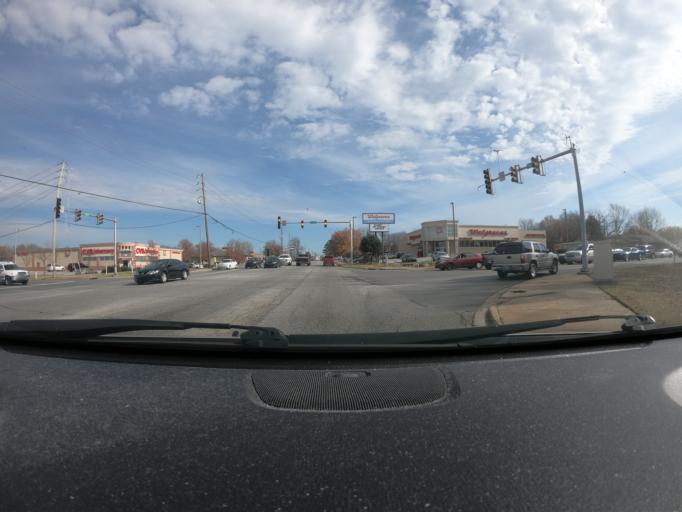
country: US
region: Arkansas
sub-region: Benton County
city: Rogers
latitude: 36.3340
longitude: -94.1442
